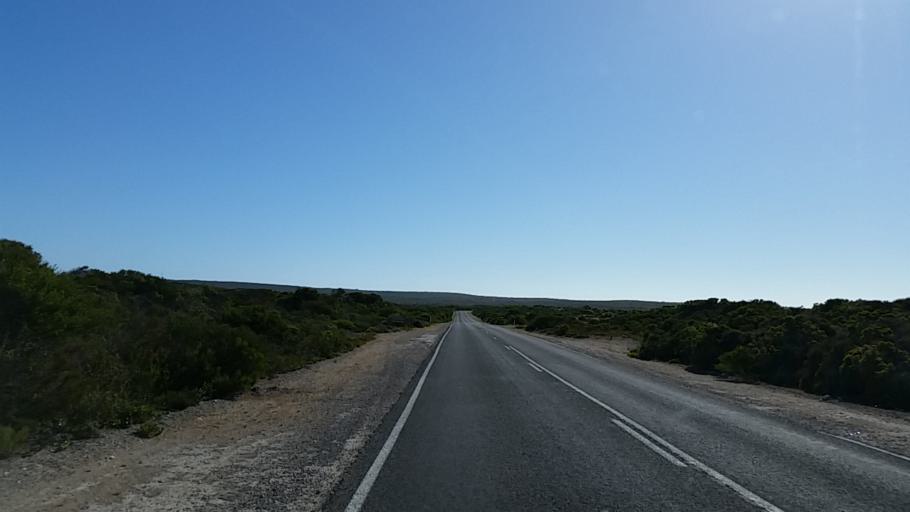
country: AU
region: South Australia
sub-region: Yorke Peninsula
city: Honiton
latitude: -35.2636
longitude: 136.9534
